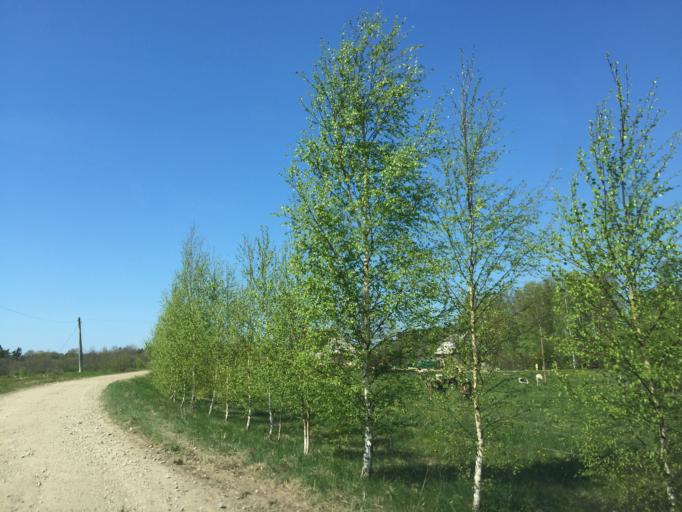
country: LV
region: Saulkrastu
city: Saulkrasti
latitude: 57.3375
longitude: 24.4817
